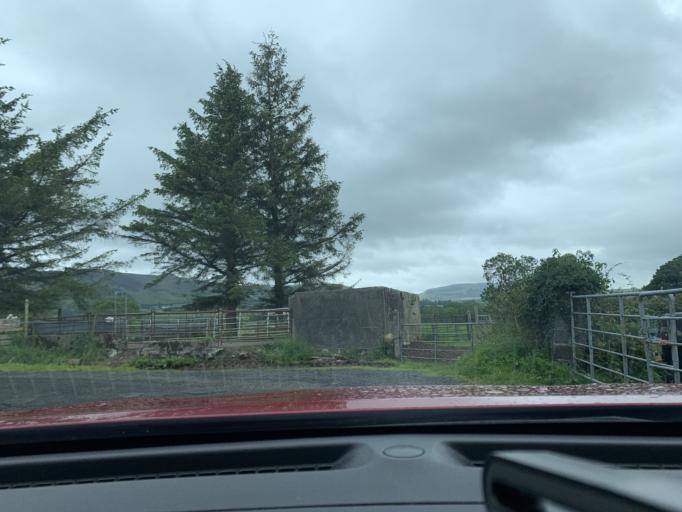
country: IE
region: Connaught
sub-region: Sligo
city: Sligo
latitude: 54.3048
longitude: -8.4458
